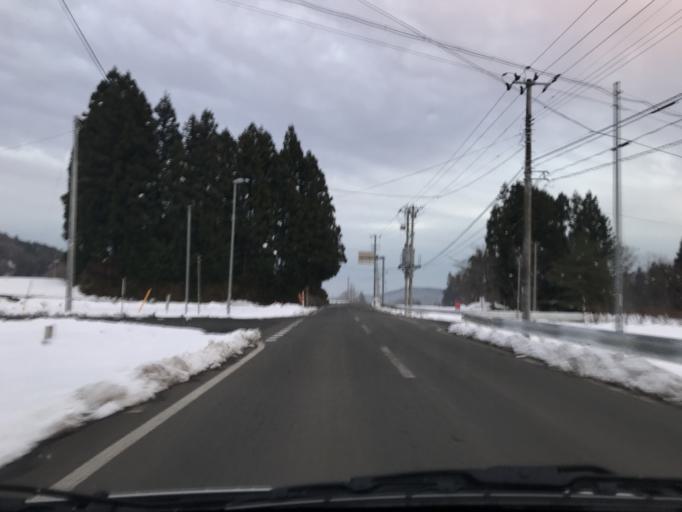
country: JP
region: Iwate
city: Mizusawa
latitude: 39.0537
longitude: 141.0442
